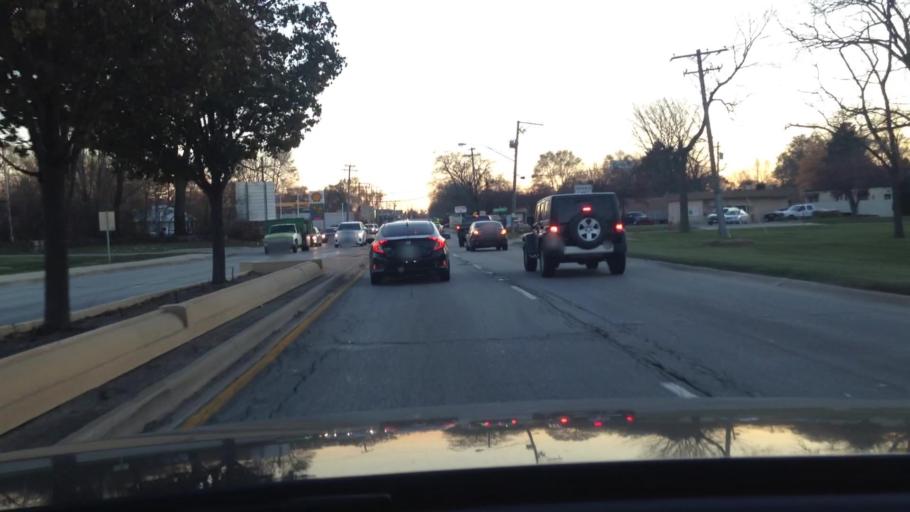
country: US
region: Illinois
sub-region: Kane County
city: Elgin
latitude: 42.0642
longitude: -88.2648
